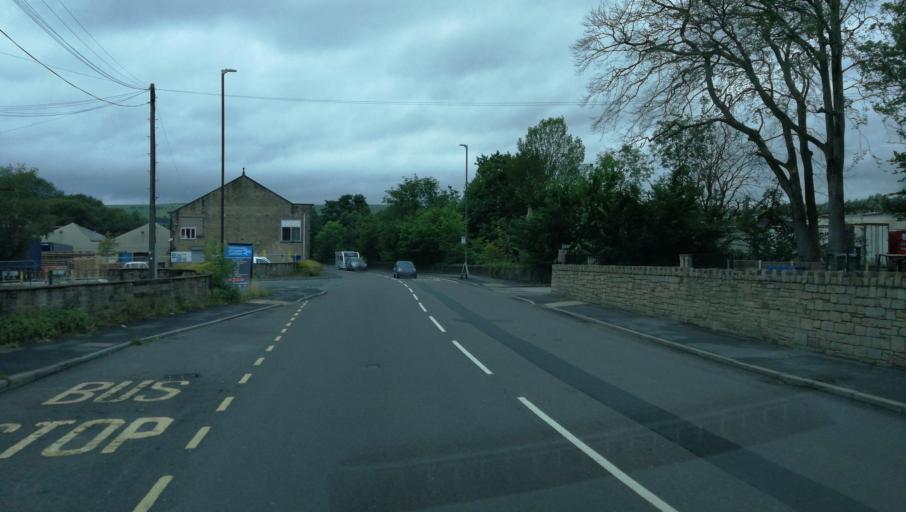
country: GB
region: England
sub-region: Borough of Tameside
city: Longdendale
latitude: 53.4492
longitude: -1.9777
